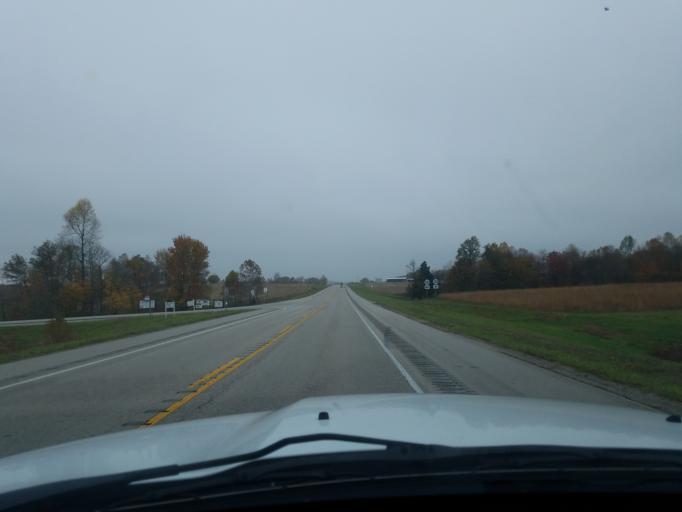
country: US
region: Kentucky
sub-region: Green County
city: Greensburg
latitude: 37.4134
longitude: -85.4939
